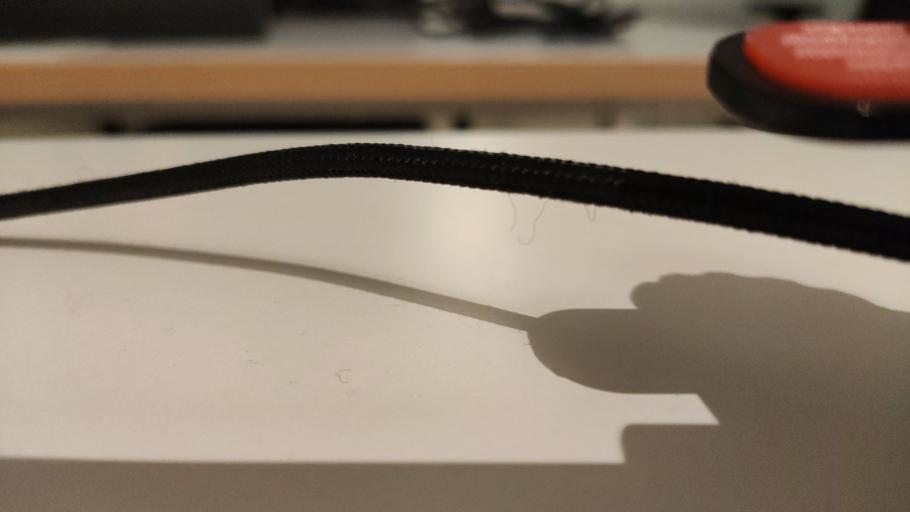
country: RU
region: Moskovskaya
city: Dmitrov
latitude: 56.3516
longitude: 37.5197
